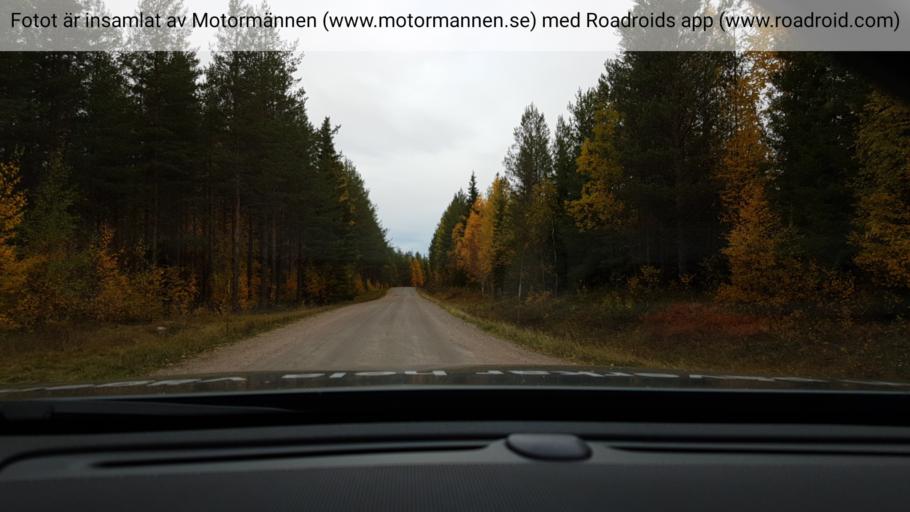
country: SE
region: Norrbotten
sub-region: Overkalix Kommun
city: OEverkalix
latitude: 66.2768
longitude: 22.9841
